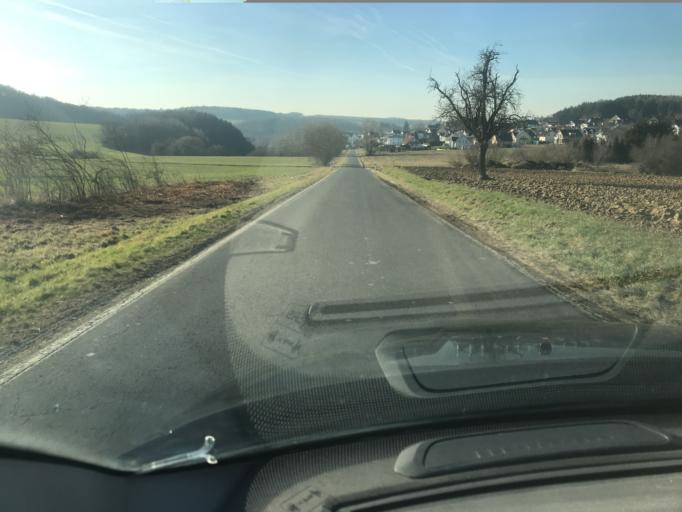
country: DE
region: Rheinland-Pfalz
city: Hundsangen
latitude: 50.4423
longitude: 7.9797
